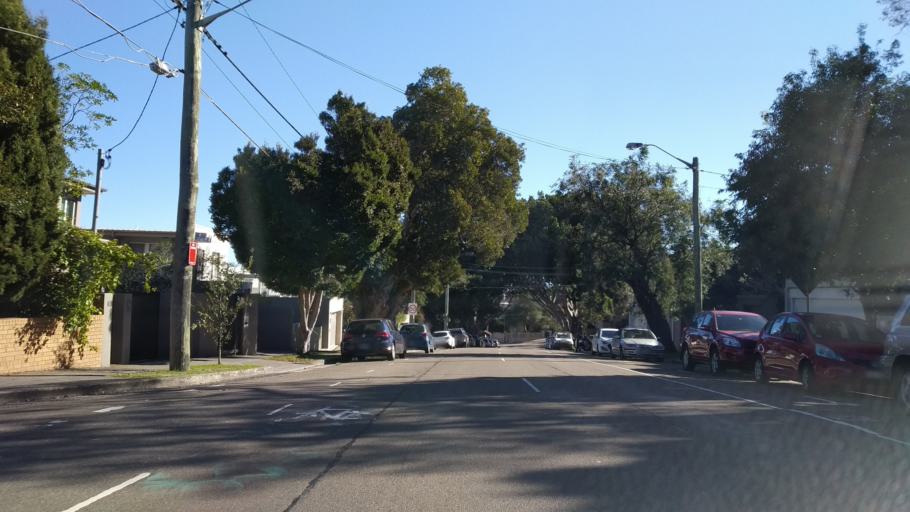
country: AU
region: New South Wales
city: Edgecliff
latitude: -33.8833
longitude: 151.2534
